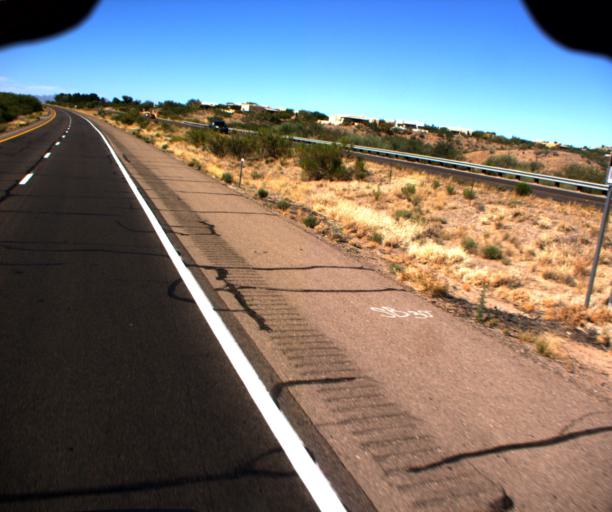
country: US
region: Arizona
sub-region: Pima County
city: Green Valley
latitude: 31.8398
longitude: -110.9984
